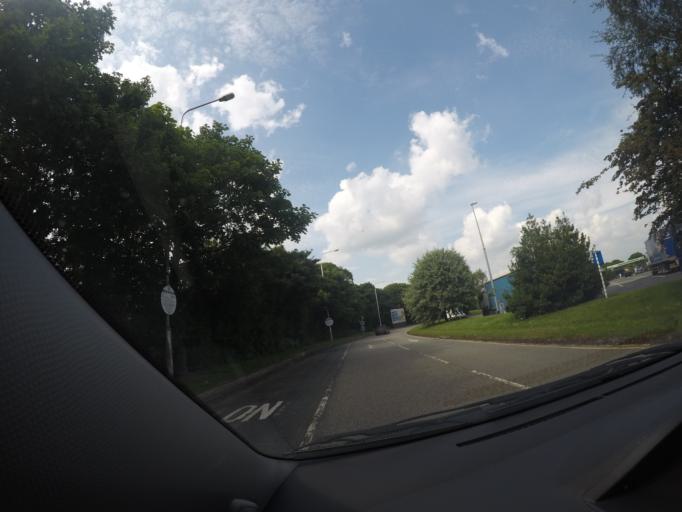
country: GB
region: England
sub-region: Cumbria
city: Scotby
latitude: 54.7980
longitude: -2.8736
